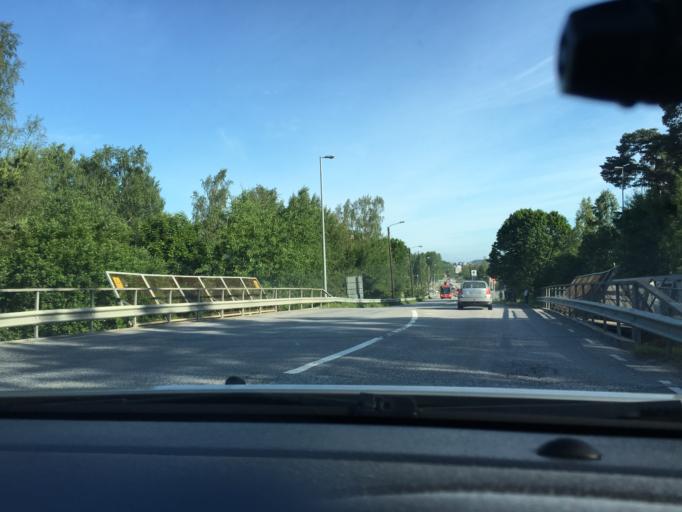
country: SE
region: Stockholm
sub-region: Sodertalje Kommun
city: Pershagen
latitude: 59.1628
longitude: 17.6418
